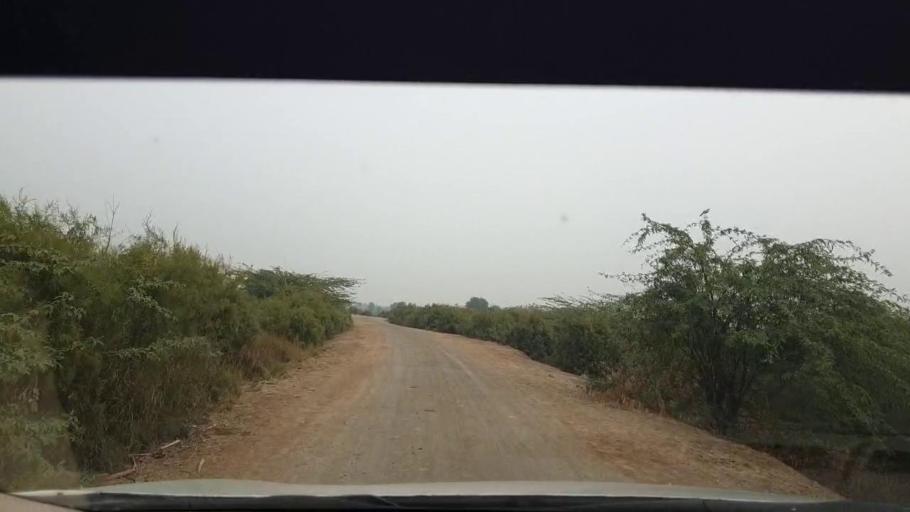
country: PK
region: Sindh
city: Berani
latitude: 25.8668
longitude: 68.8270
